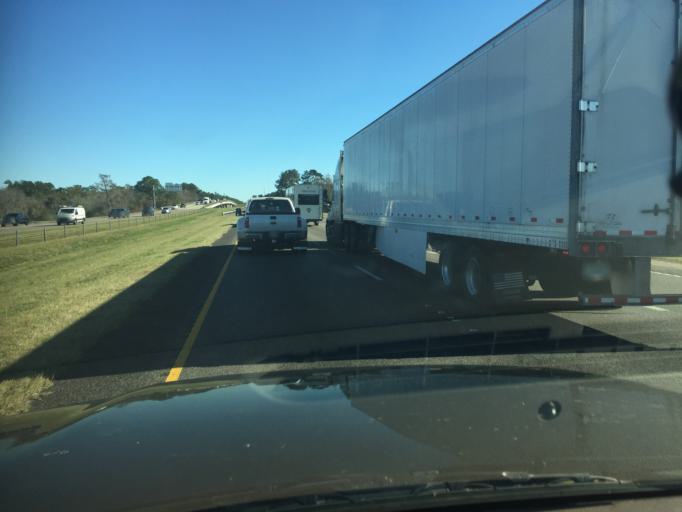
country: US
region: Louisiana
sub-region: Saint Tammany Parish
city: Covington
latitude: 30.4406
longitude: -90.1218
